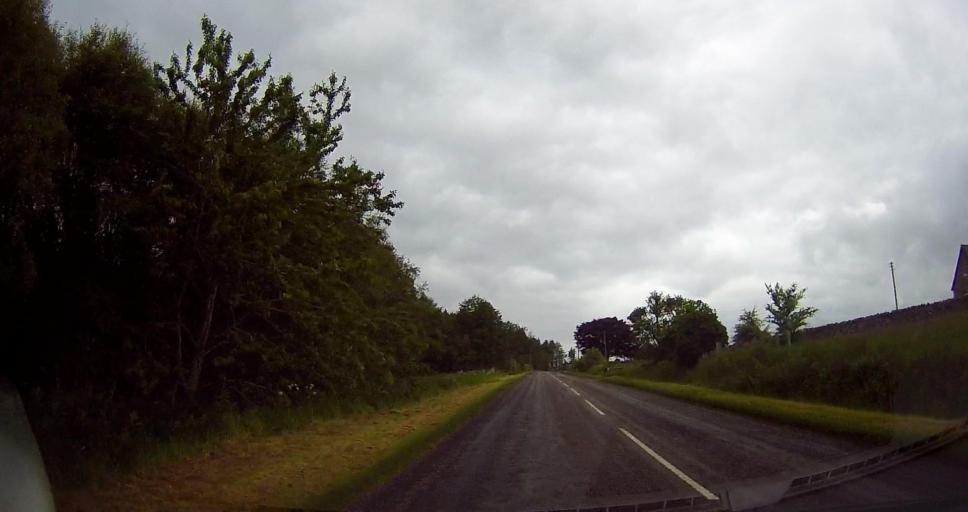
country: GB
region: Scotland
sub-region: Highland
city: Alness
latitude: 58.0209
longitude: -4.3732
